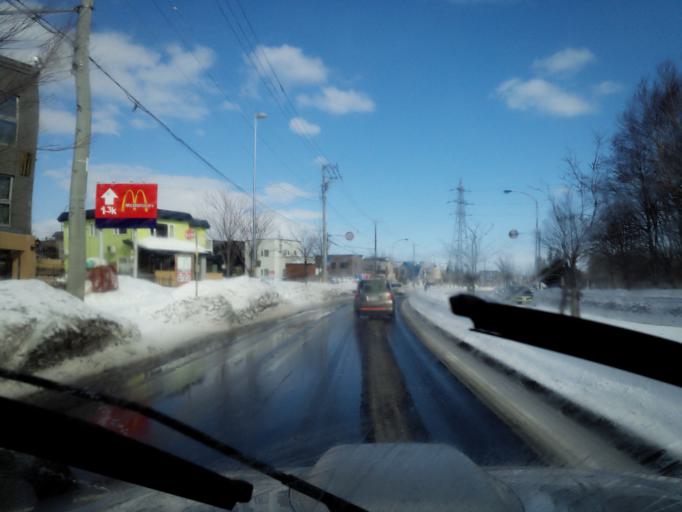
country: JP
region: Hokkaido
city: Kitahiroshima
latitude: 43.0026
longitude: 141.4599
